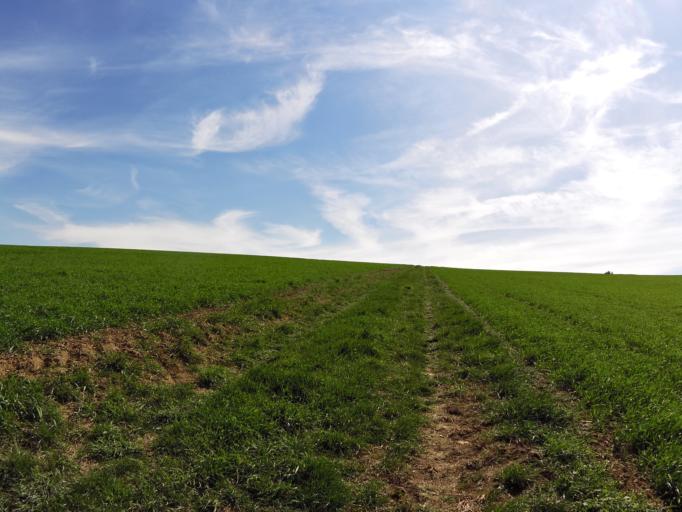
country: DE
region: Bavaria
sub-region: Regierungsbezirk Unterfranken
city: Rottendorf
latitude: 49.7996
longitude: 10.0394
